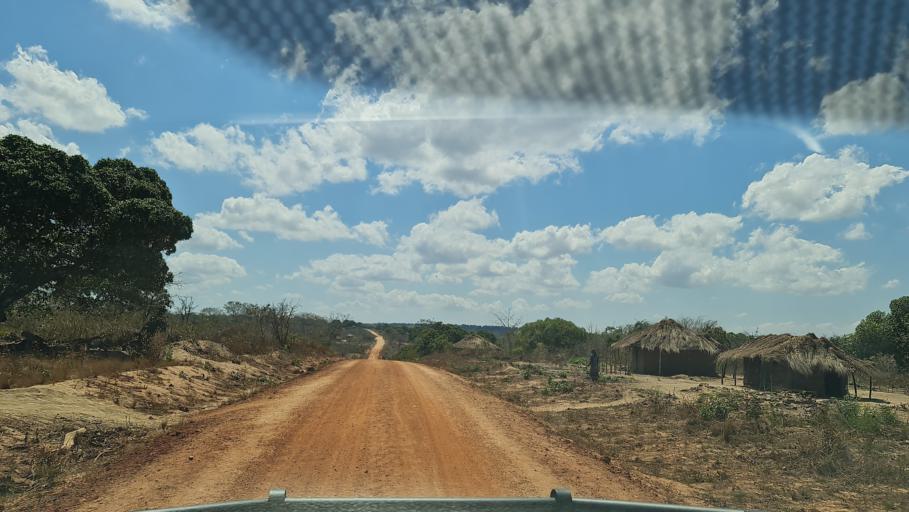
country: MZ
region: Nampula
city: Nacala
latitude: -14.1759
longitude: 40.2313
